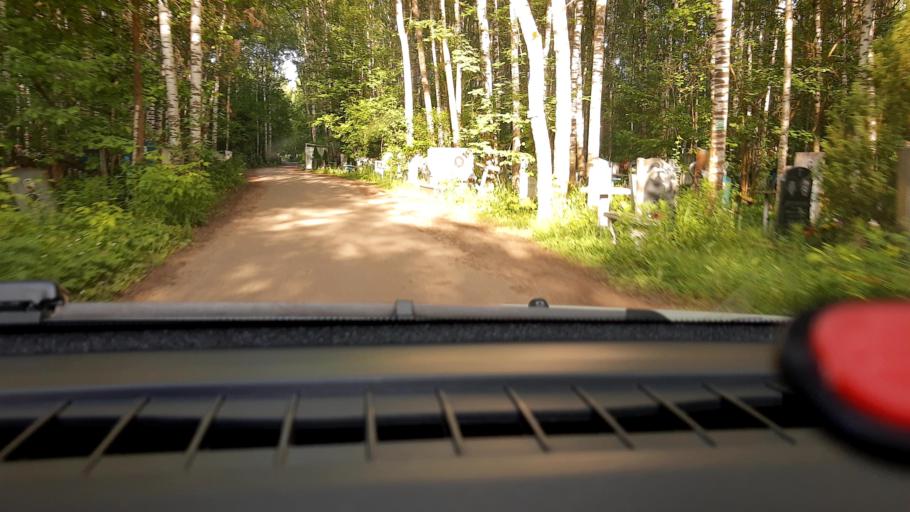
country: RU
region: Nizjnij Novgorod
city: Gorbatovka
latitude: 56.2322
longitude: 43.7708
